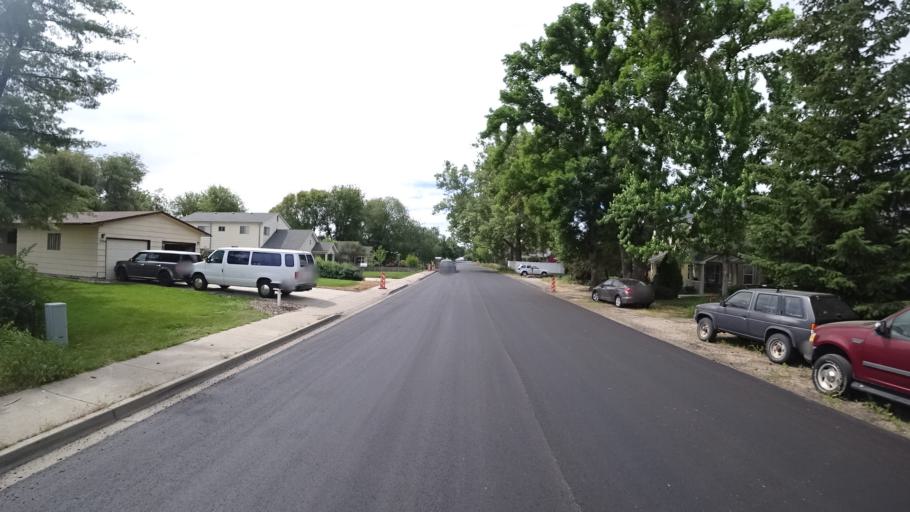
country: US
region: Idaho
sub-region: Ada County
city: Boise
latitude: 43.5915
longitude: -116.1885
